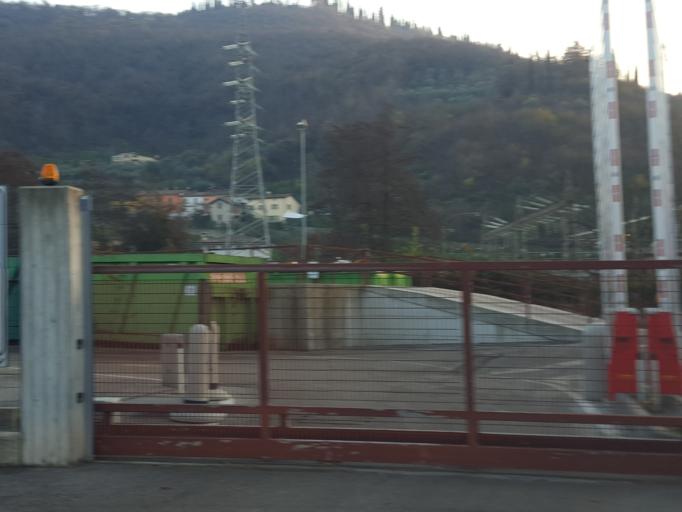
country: IT
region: Veneto
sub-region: Provincia di Verona
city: Garda
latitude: 45.5764
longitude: 10.7190
